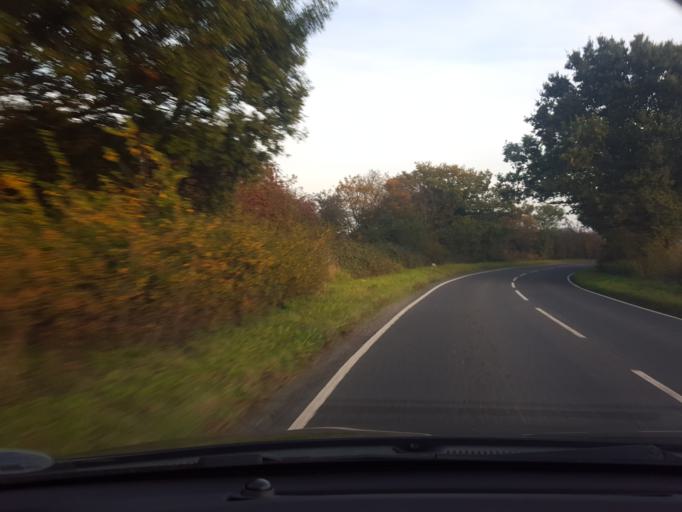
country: GB
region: England
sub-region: Essex
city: Little Clacton
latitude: 51.8307
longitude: 1.1575
